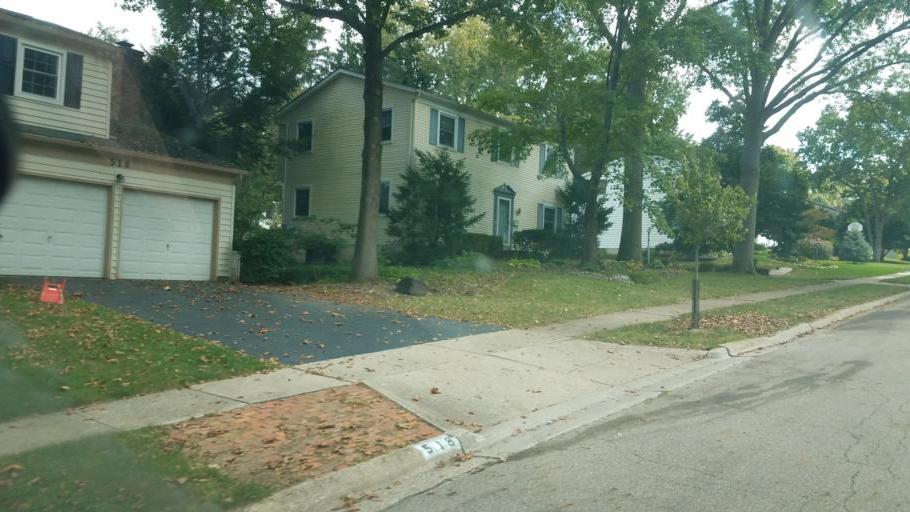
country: US
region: Ohio
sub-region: Franklin County
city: Worthington
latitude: 40.1050
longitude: -83.0314
